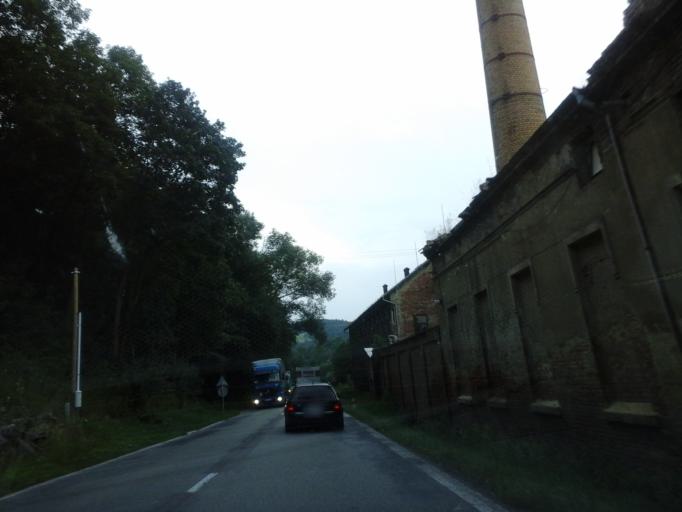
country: CZ
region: Pardubicky
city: Brnenec
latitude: 49.6094
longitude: 16.5321
